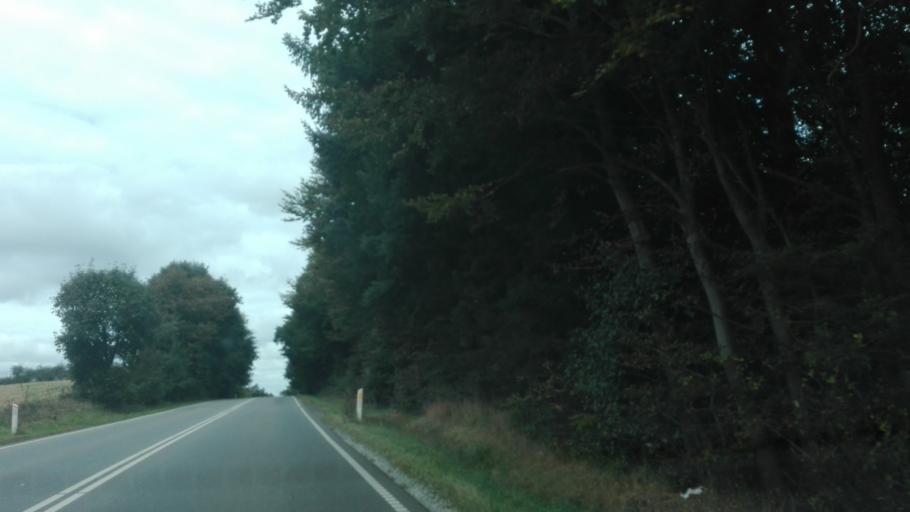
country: DK
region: Central Jutland
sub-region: Skanderborg Kommune
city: Stilling
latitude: 56.1000
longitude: 9.9706
